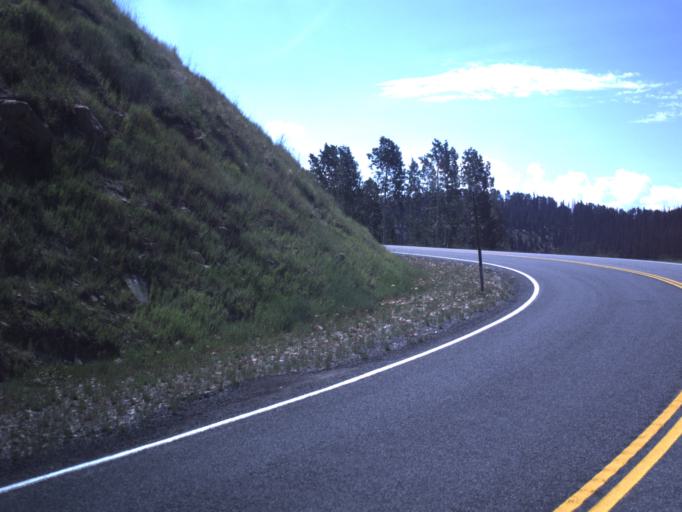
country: US
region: Utah
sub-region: Sanpete County
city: Fairview
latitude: 39.6807
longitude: -111.2314
